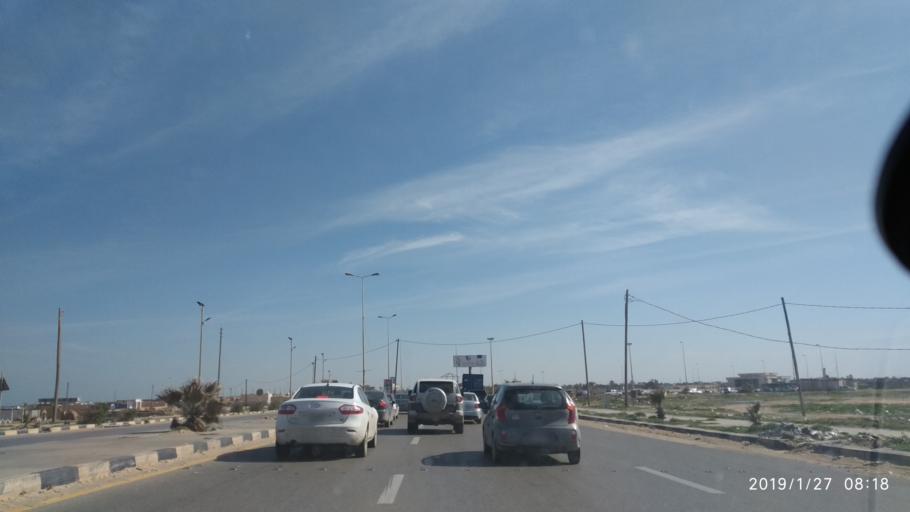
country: LY
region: Tripoli
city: Tagiura
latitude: 32.8967
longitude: 13.3208
